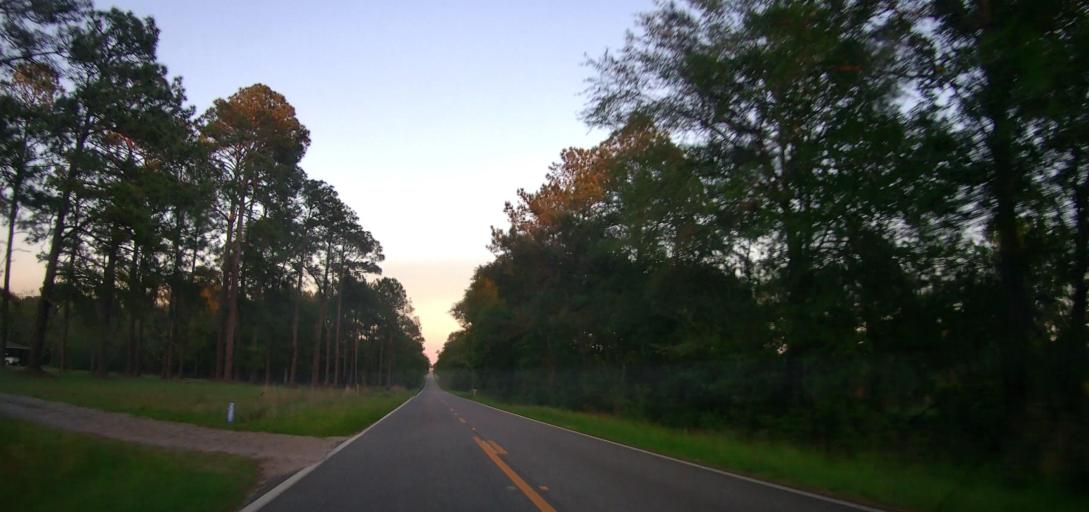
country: US
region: Georgia
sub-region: Wilcox County
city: Rochelle
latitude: 31.7831
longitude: -83.4281
